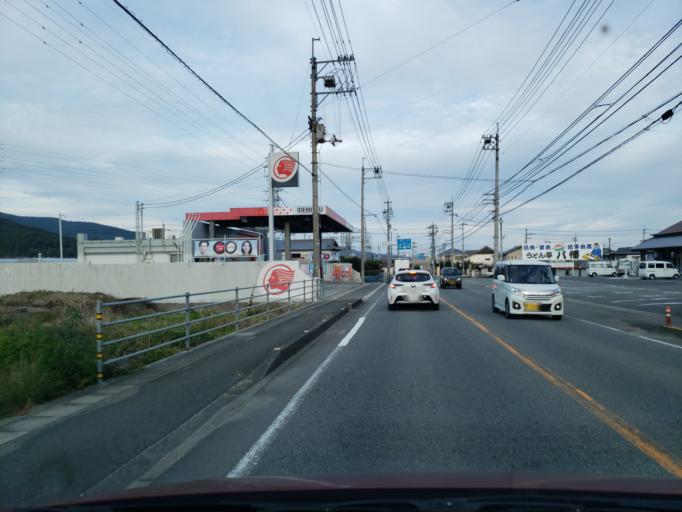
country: JP
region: Tokushima
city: Kamojimacho-jogejima
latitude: 34.0928
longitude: 134.3076
